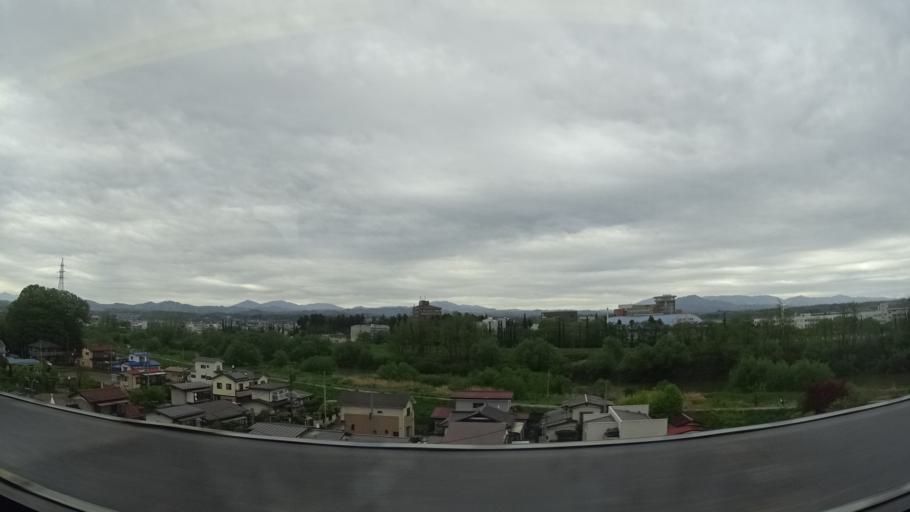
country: JP
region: Fukushima
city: Koriyama
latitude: 37.3619
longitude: 140.3766
